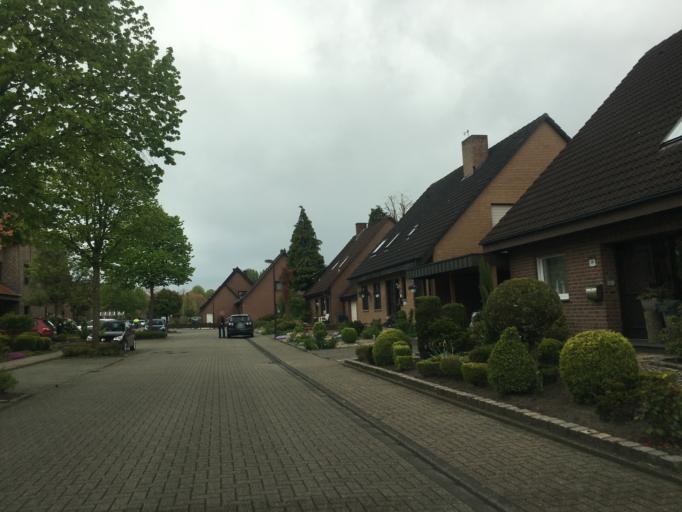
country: DE
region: North Rhine-Westphalia
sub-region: Regierungsbezirk Munster
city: Nordwalde
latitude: 52.0842
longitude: 7.4913
